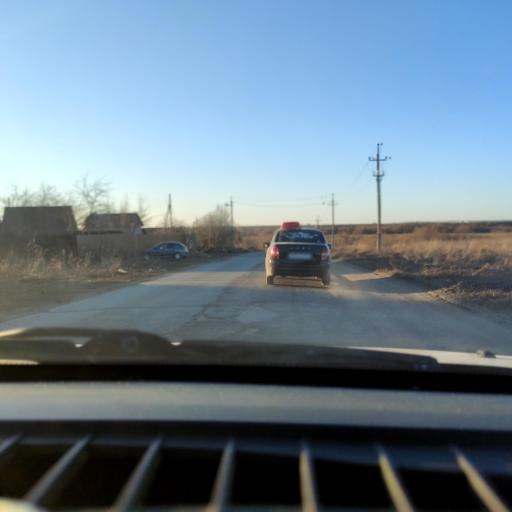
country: RU
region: Perm
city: Kultayevo
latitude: 57.9373
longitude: 56.0122
